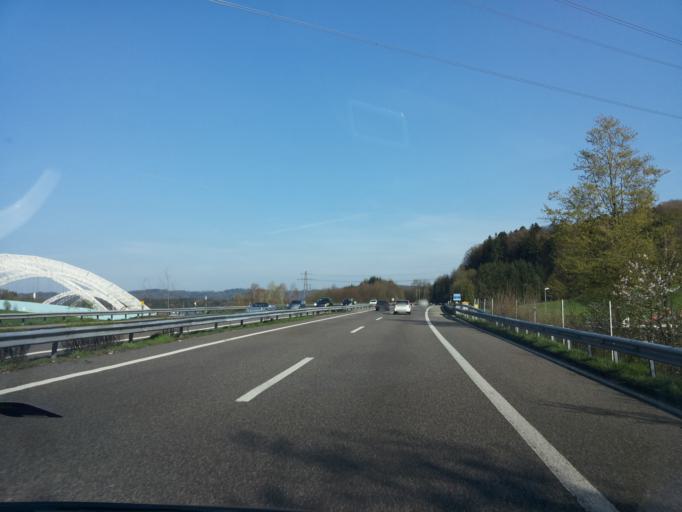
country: CH
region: Aargau
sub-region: Bezirk Zofingen
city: Safenwil
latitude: 47.3233
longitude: 8.0045
